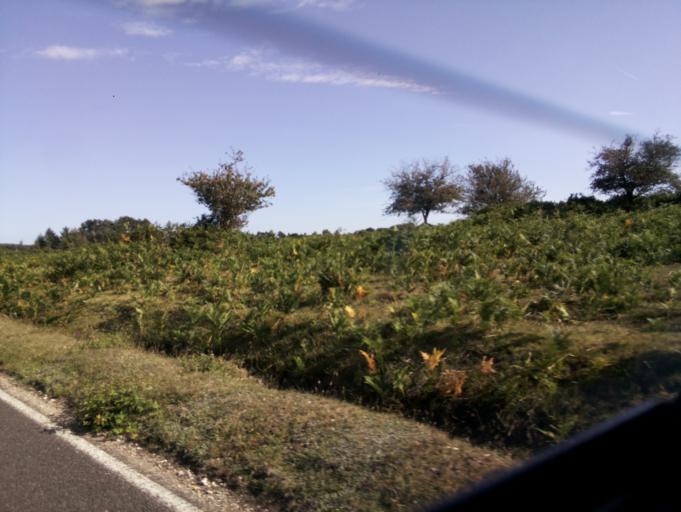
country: GB
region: England
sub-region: Hampshire
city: Cadnam
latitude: 50.9065
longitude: -1.6399
